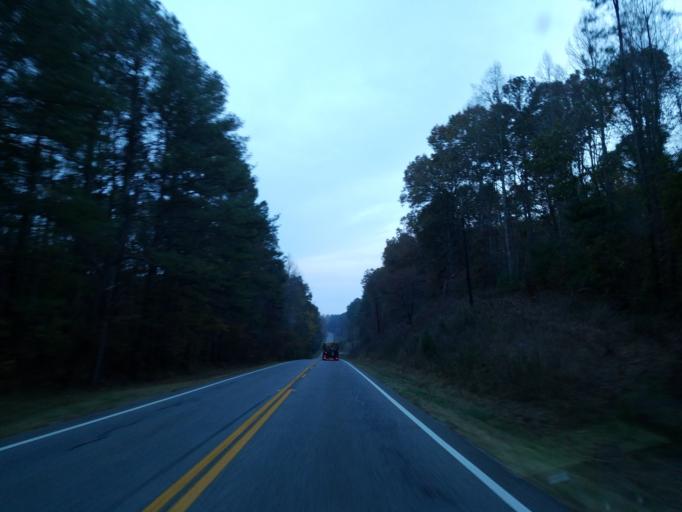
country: US
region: Georgia
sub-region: Pickens County
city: Jasper
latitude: 34.5218
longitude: -84.5703
